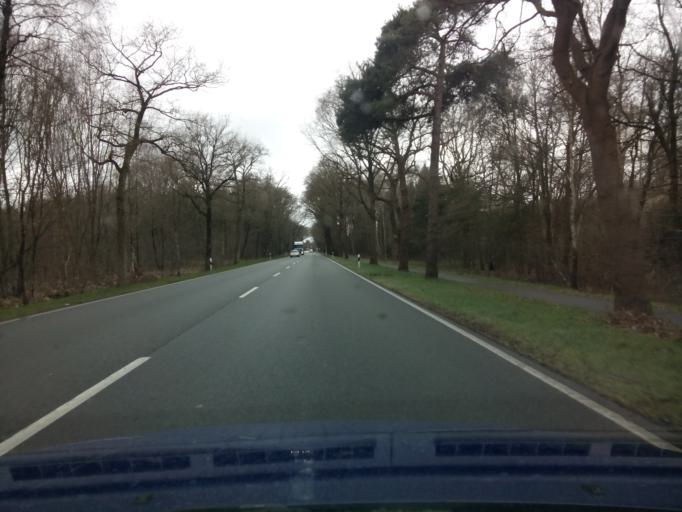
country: DE
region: Lower Saxony
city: Meppen
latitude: 52.7056
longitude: 7.3650
